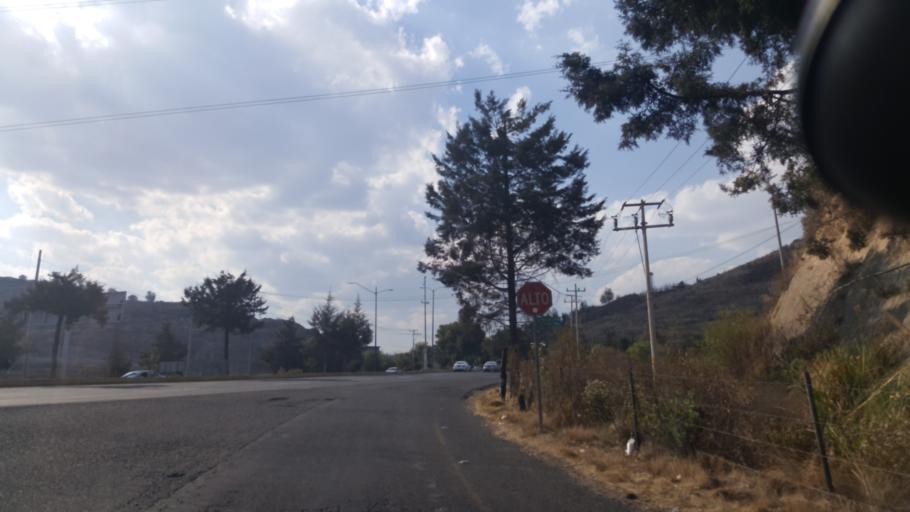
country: MX
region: Mexico
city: Ciudad Lopez Mateos
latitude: 19.5472
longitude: -99.2791
